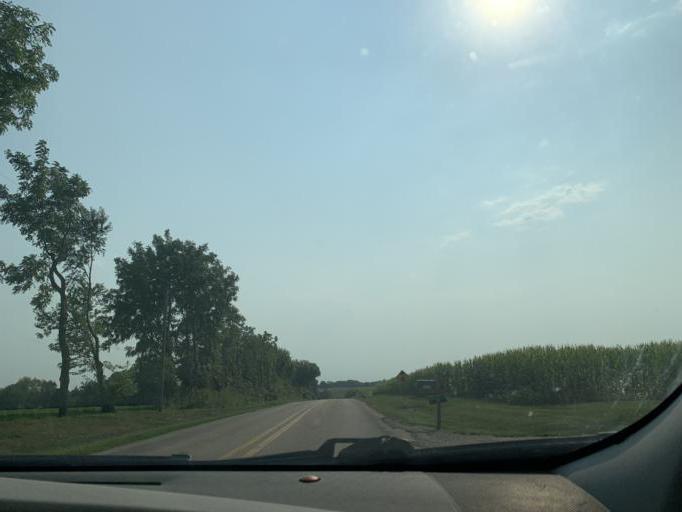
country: US
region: Illinois
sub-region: Carroll County
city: Milledgeville
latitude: 41.8479
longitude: -89.8090
